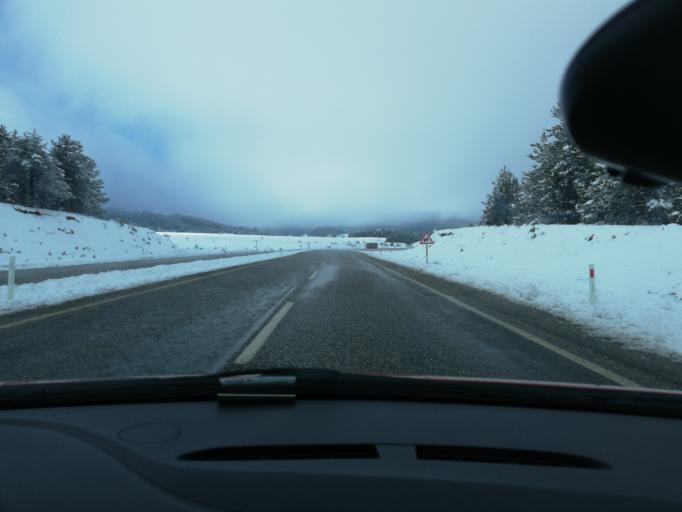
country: TR
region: Kastamonu
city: Ihsangazi
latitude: 41.3037
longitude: 33.5611
